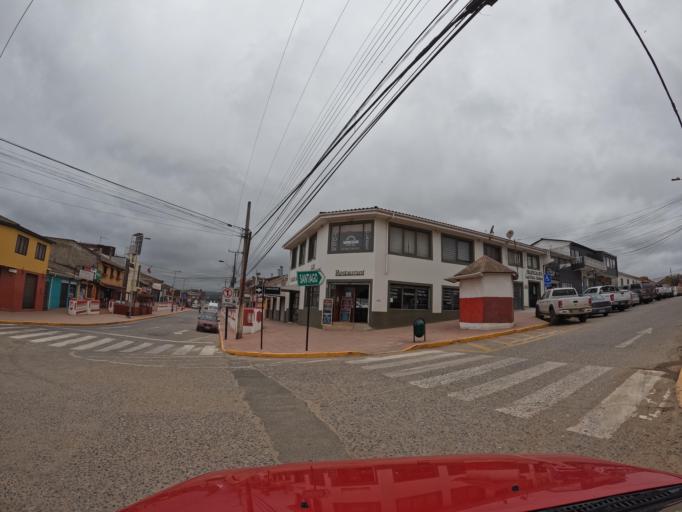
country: CL
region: O'Higgins
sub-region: Provincia de Colchagua
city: Santa Cruz
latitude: -34.3876
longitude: -72.0065
